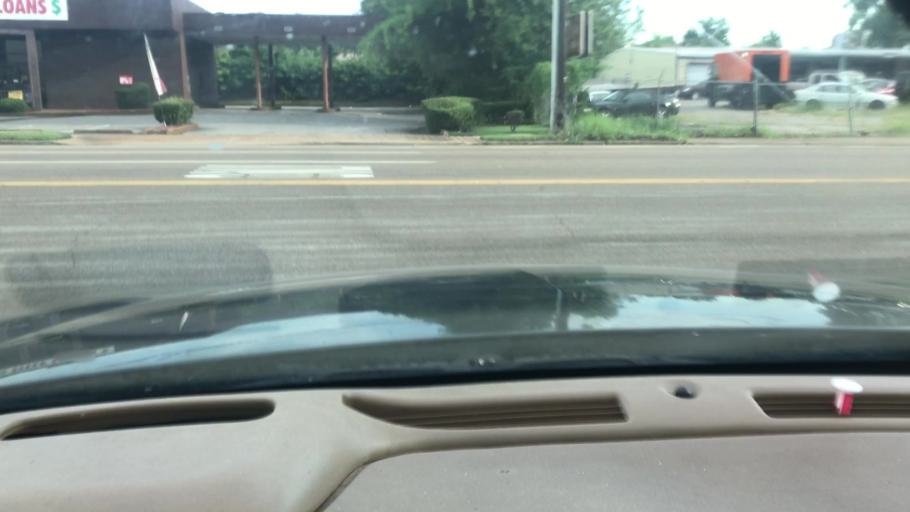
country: US
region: Tennessee
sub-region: Shelby County
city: New South Memphis
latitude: 35.0612
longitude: -90.0078
